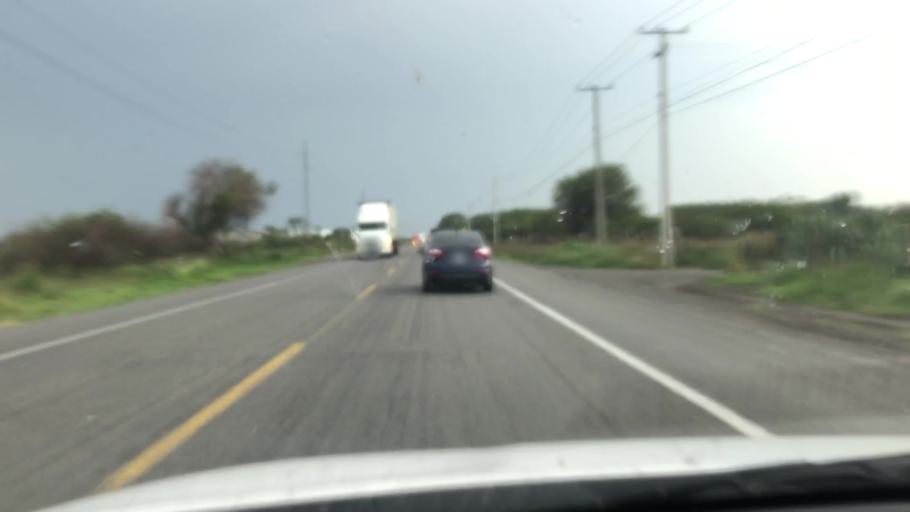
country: MX
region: Michoacan
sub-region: Vista Hermosa
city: Los Pilares
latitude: 20.2740
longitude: -102.4071
